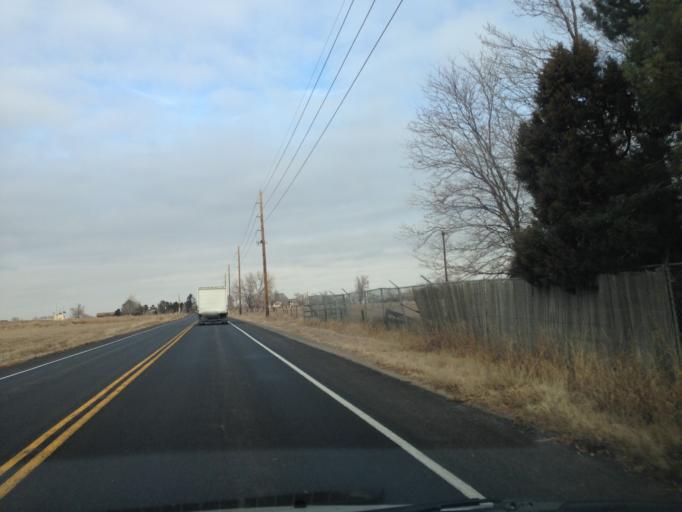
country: US
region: Colorado
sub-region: Boulder County
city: Lafayette
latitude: 40.0021
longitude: -105.0745
